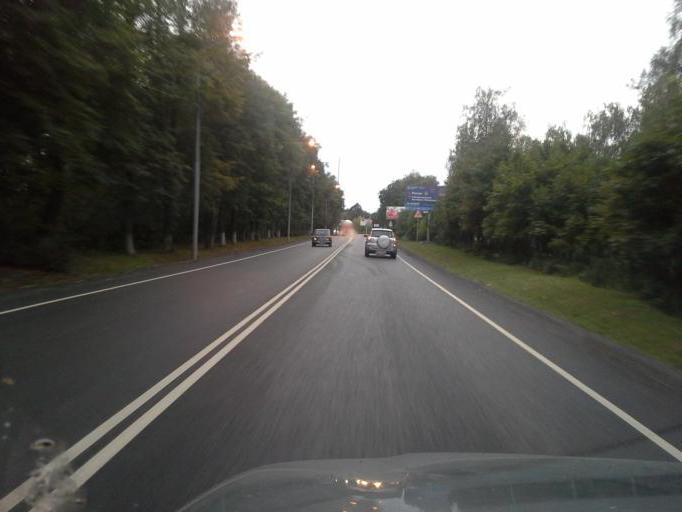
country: RU
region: Moskovskaya
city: Nikolina Gora
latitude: 55.7142
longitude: 37.0735
